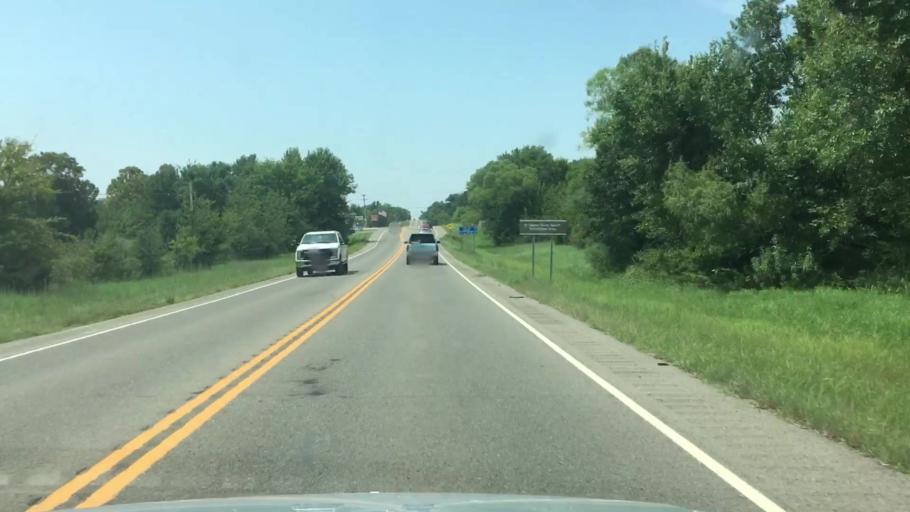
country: US
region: Oklahoma
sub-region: Wagoner County
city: Wagoner
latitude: 35.9415
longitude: -95.2942
